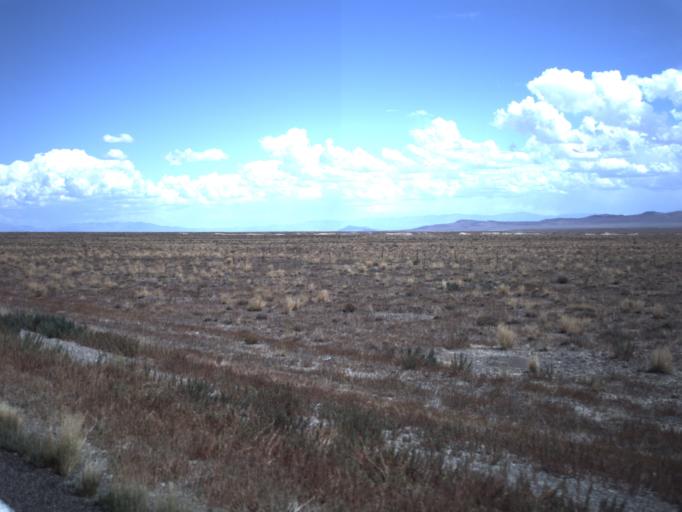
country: US
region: Utah
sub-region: Millard County
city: Delta
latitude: 39.1373
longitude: -113.0913
